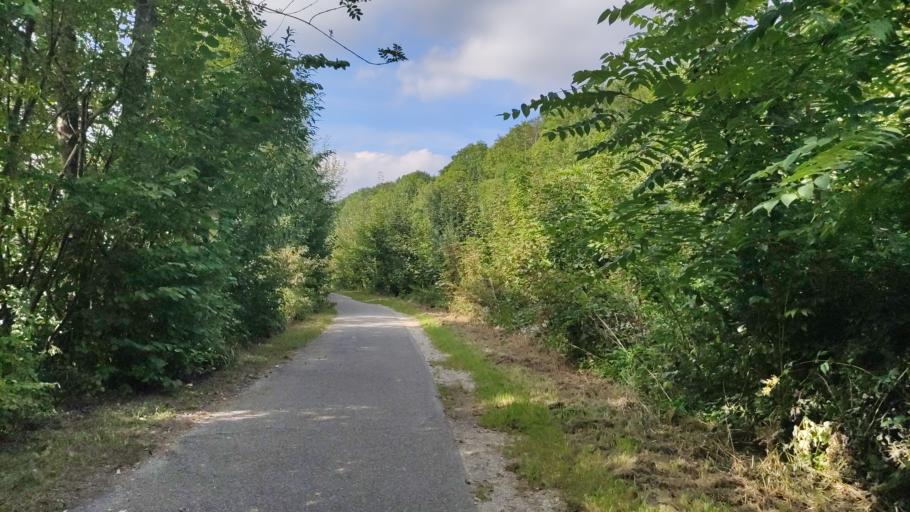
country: DE
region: Bavaria
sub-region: Upper Bavaria
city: Kaufering
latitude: 48.1092
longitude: 10.8690
